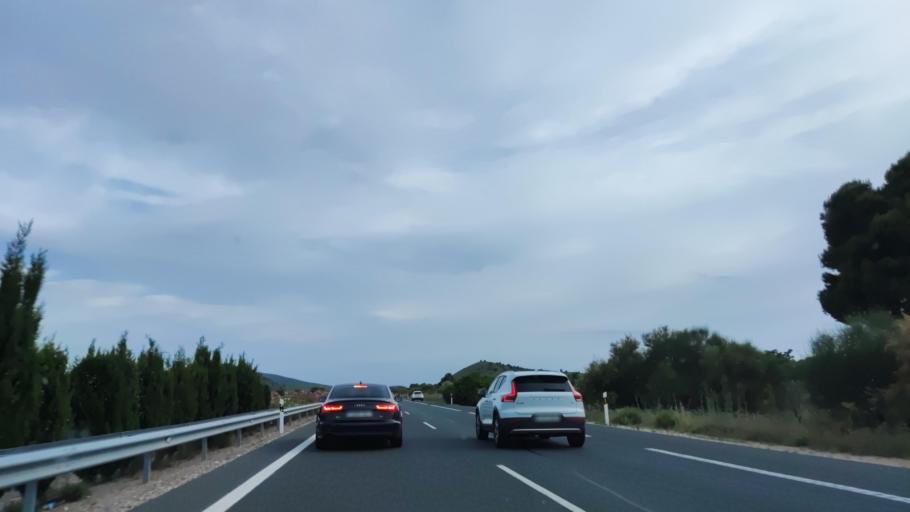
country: ES
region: Castille-La Mancha
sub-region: Provincia de Albacete
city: Tobarra
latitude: 38.6538
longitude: -1.6630
